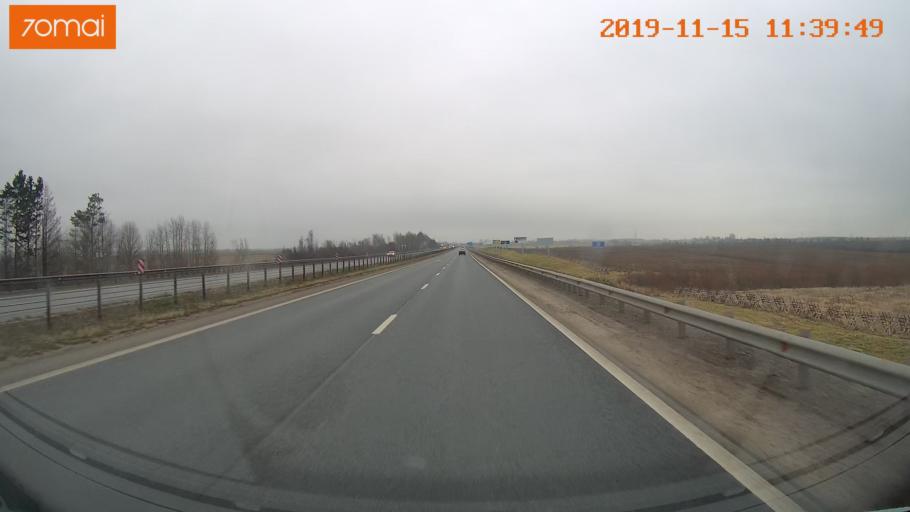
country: RU
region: Vologda
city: Molochnoye
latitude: 59.2119
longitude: 39.7344
